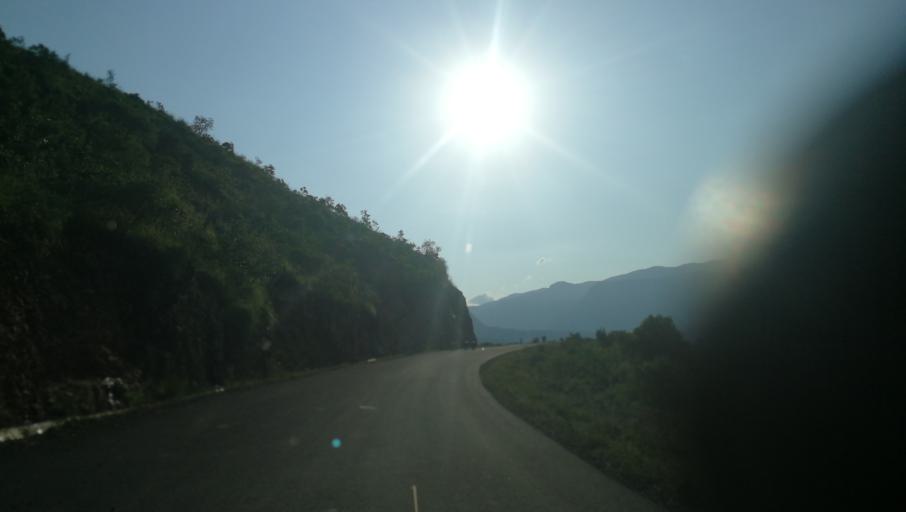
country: ET
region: Southern Nations, Nationalities, and People's Region
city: Areka
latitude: 6.8317
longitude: 37.3133
